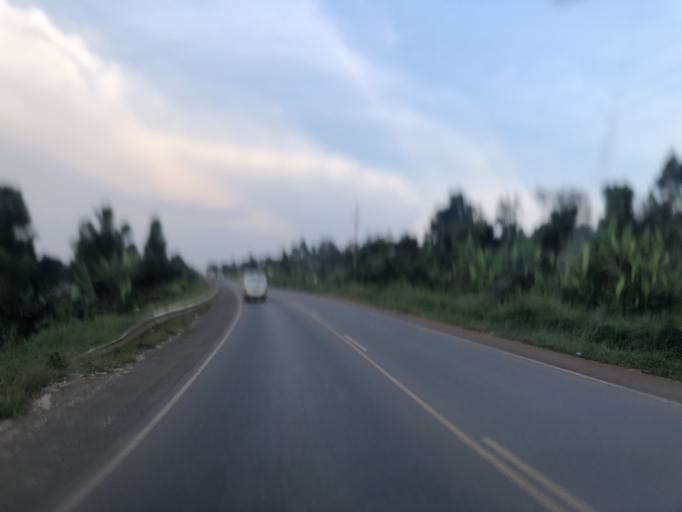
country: UG
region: Central Region
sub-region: Mpigi District
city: Mpigi
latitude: 0.2286
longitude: 32.3441
